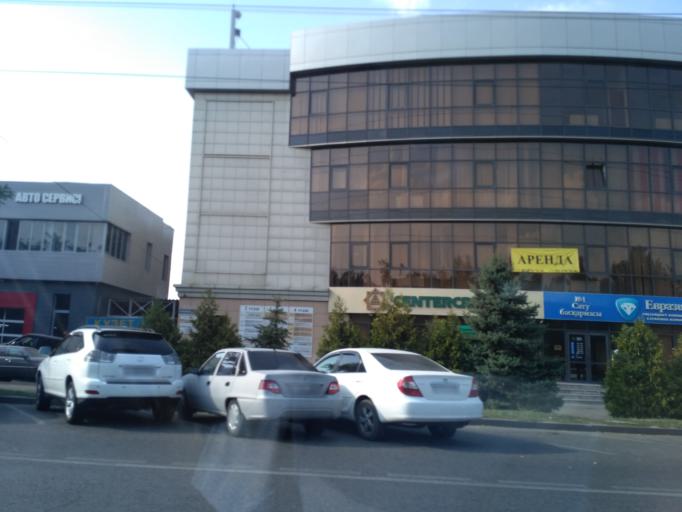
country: KZ
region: Almaty Qalasy
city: Almaty
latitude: 43.2630
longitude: 76.8972
